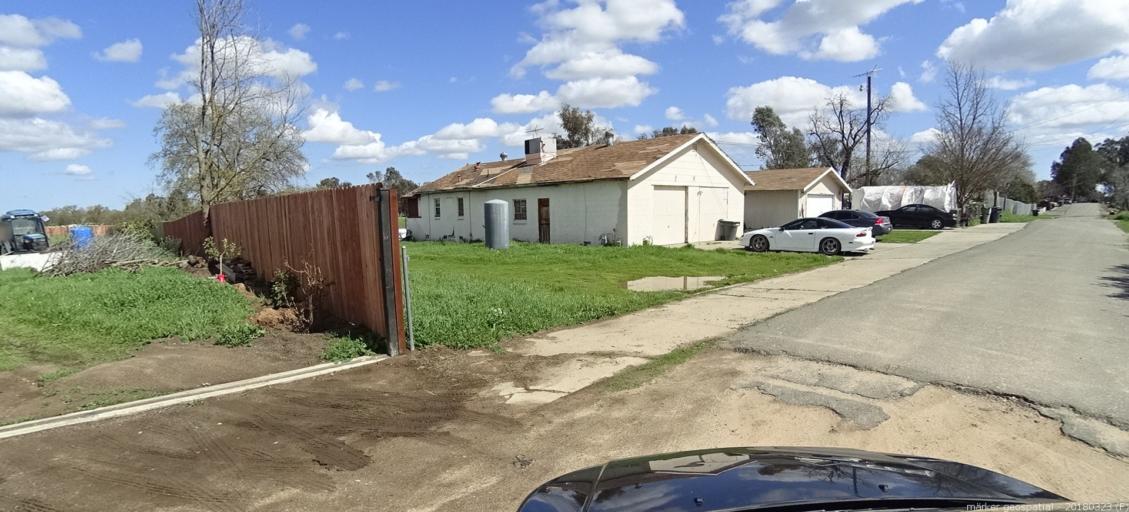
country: US
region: California
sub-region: Sacramento County
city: Rio Linda
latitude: 38.6890
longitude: -121.4269
